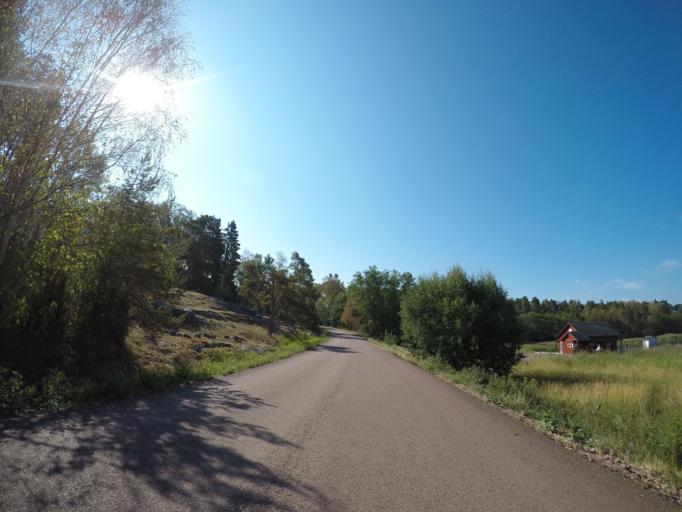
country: AX
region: Alands landsbygd
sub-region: Finstroem
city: Finstroem
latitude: 60.3291
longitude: 19.9127
